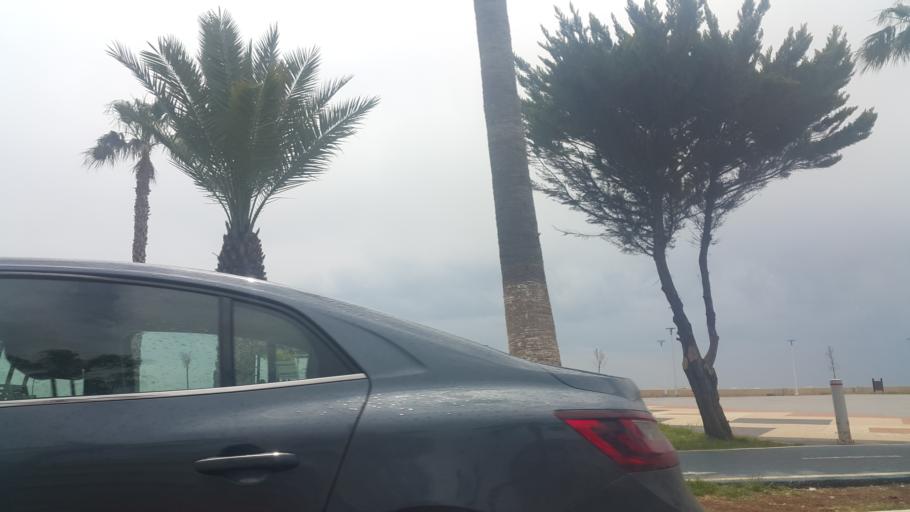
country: TR
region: Mersin
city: Mercin
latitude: 36.7769
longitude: 34.5831
